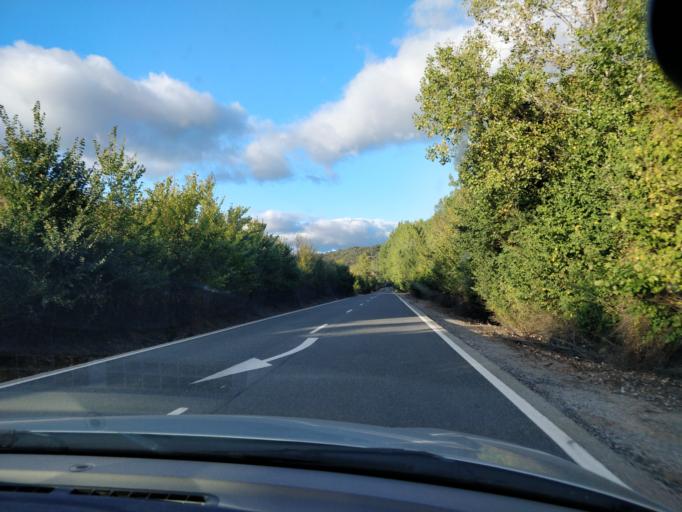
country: ES
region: Castille and Leon
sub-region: Provincia de Leon
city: Borrenes
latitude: 42.4969
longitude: -6.7357
